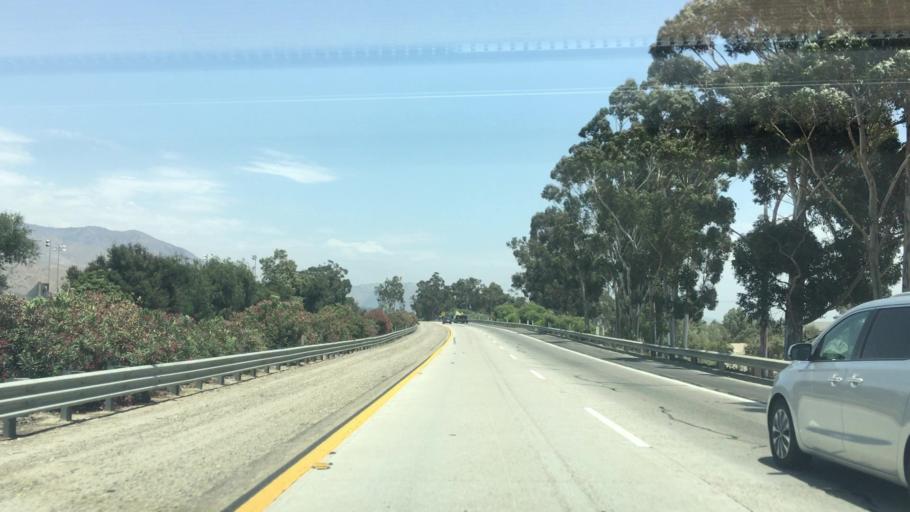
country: US
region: California
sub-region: Ventura County
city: Santa Paula
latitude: 34.3530
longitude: -119.0514
